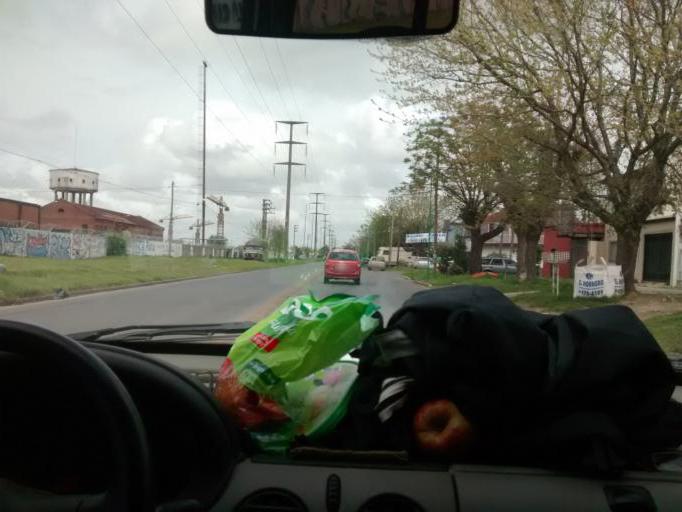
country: AR
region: Buenos Aires
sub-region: Partido de La Plata
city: La Plata
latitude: -34.9421
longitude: -57.9772
